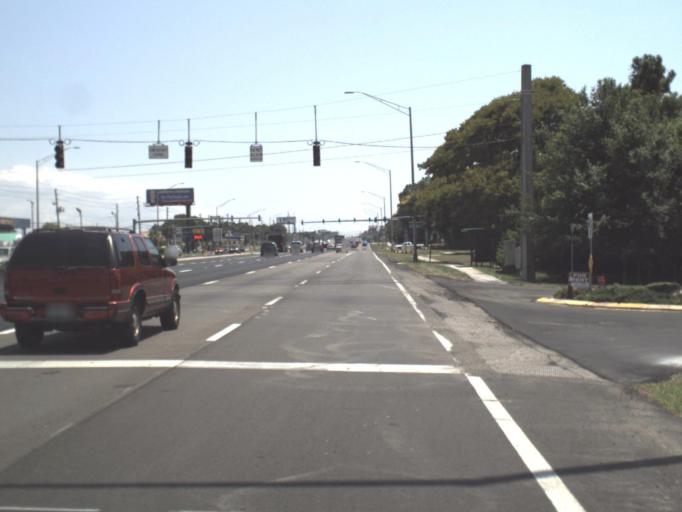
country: US
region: Florida
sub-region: Pinellas County
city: Palm Harbor
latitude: 28.1085
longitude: -82.7400
